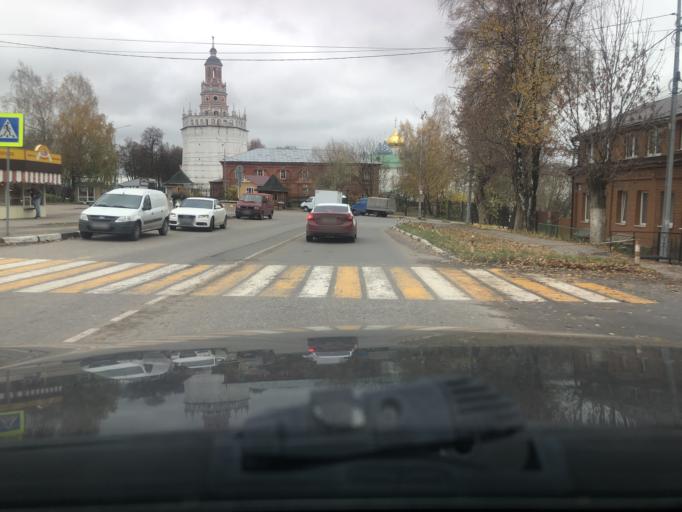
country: RU
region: Moskovskaya
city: Sergiyev Posad
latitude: 56.3141
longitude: 38.1315
